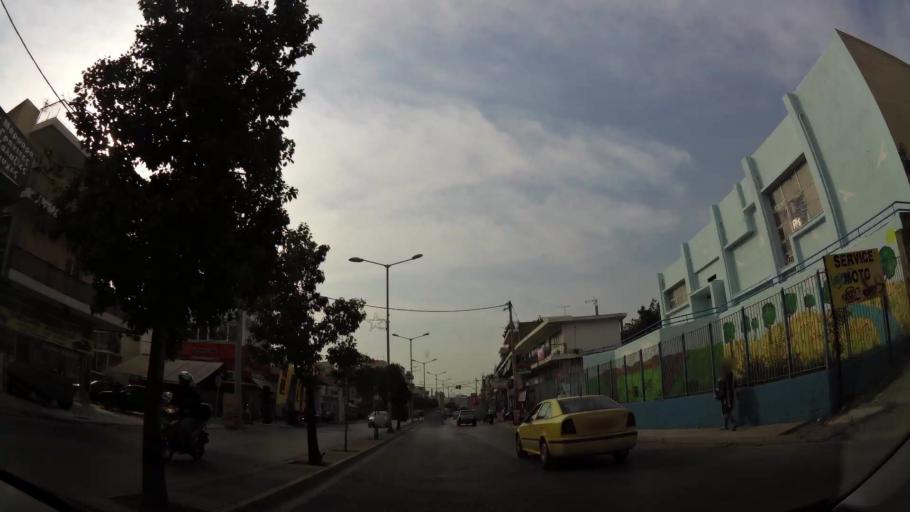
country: GR
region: Attica
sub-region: Nomarchia Athinas
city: Peristeri
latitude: 38.0090
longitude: 23.6882
